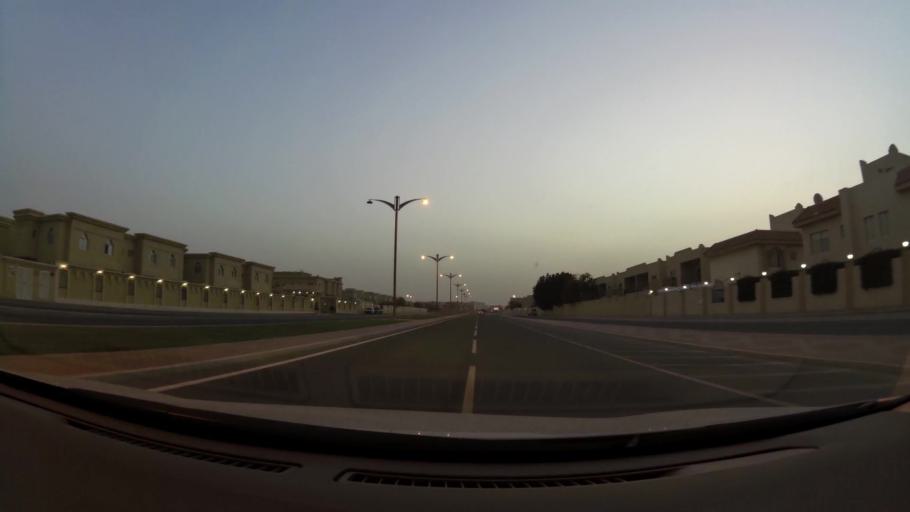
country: QA
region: Baladiyat ar Rayyan
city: Ar Rayyan
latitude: 25.2561
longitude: 51.4601
